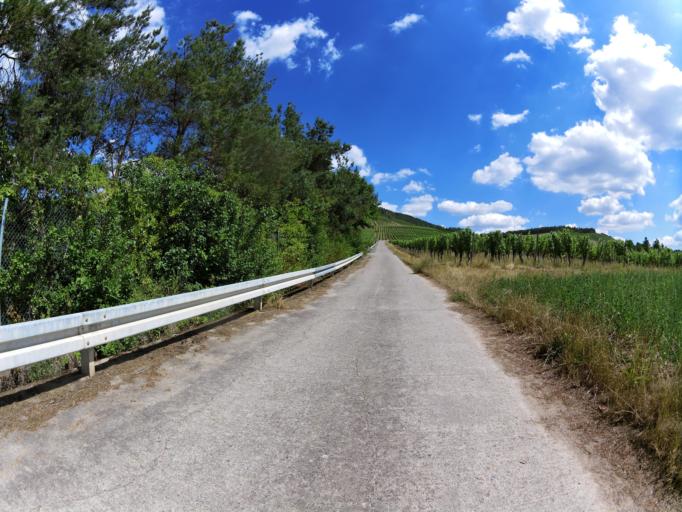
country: DE
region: Bavaria
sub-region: Regierungsbezirk Unterfranken
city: Thungersheim
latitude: 49.8861
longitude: 9.8464
